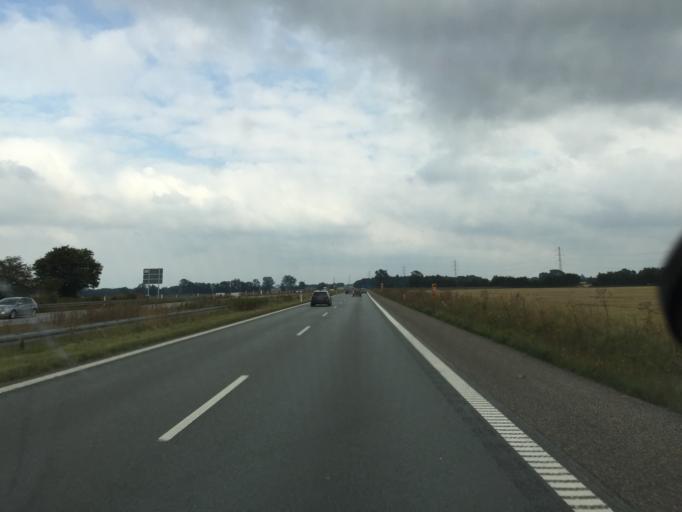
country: DK
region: Zealand
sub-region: Koge Kommune
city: Borup
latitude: 55.4577
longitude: 11.9518
